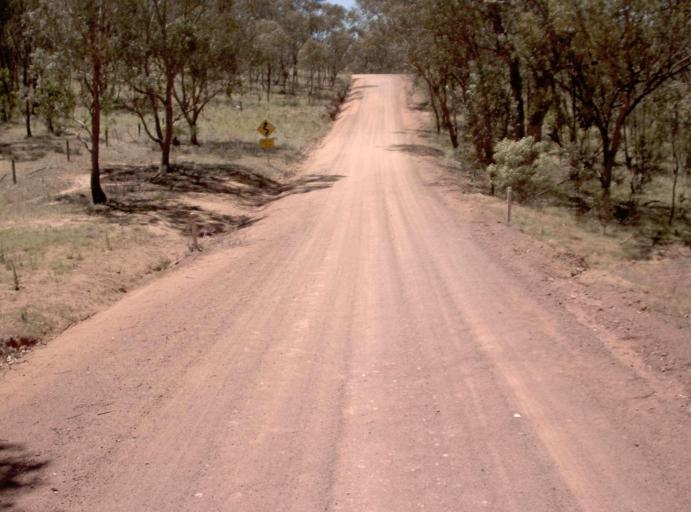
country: AU
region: New South Wales
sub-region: Snowy River
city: Jindabyne
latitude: -36.9369
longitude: 148.3477
